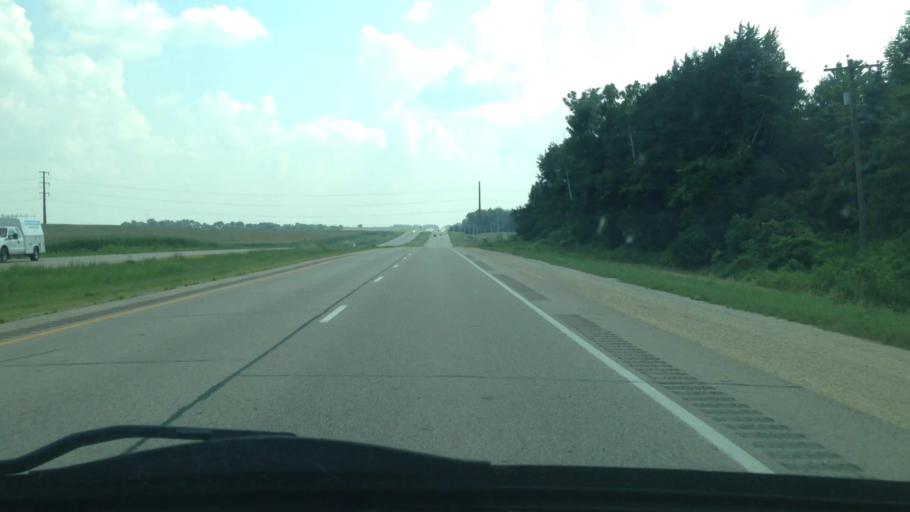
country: US
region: Iowa
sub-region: Bremer County
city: Denver
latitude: 42.5988
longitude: -92.3374
